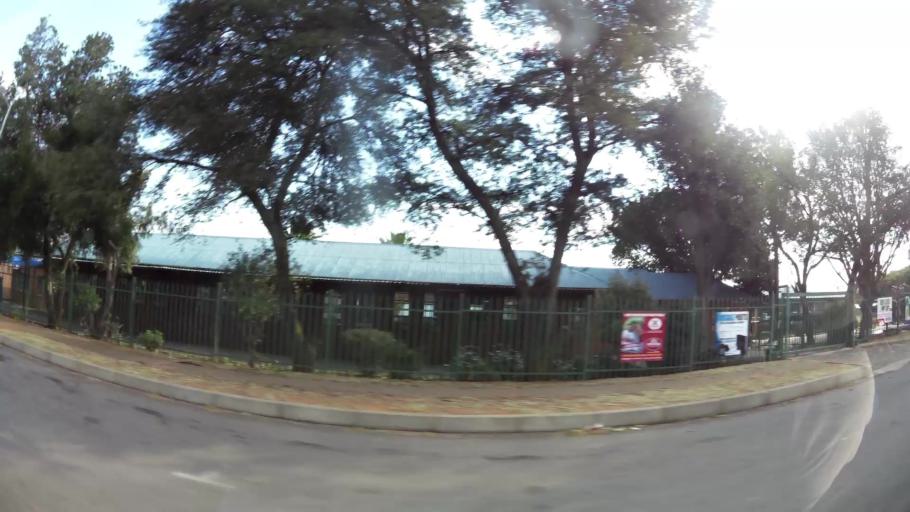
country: ZA
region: Gauteng
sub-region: West Rand District Municipality
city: Krugersdorp
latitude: -26.0900
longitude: 27.7709
